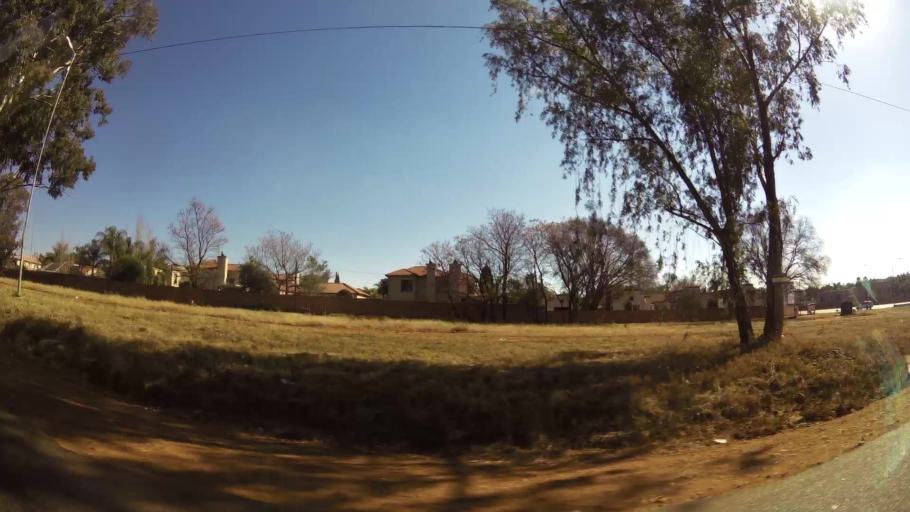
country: ZA
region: Gauteng
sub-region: City of Tshwane Metropolitan Municipality
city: Centurion
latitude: -25.8631
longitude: 28.1628
